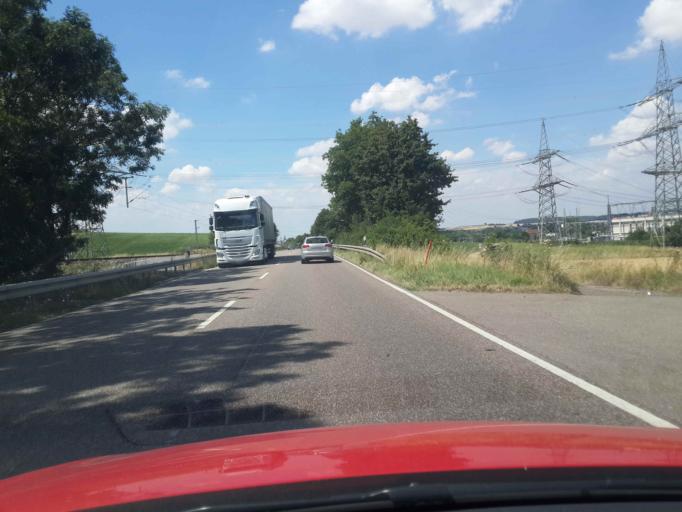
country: DE
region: Baden-Wuerttemberg
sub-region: Regierungsbezirk Stuttgart
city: Leingarten
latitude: 49.1409
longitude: 9.1512
